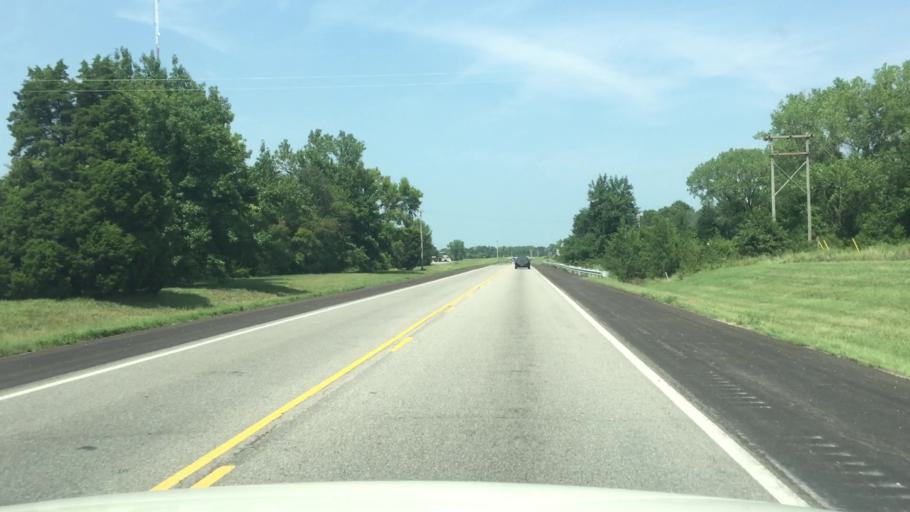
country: US
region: Kansas
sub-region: Crawford County
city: Pittsburg
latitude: 37.4290
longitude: -94.7142
